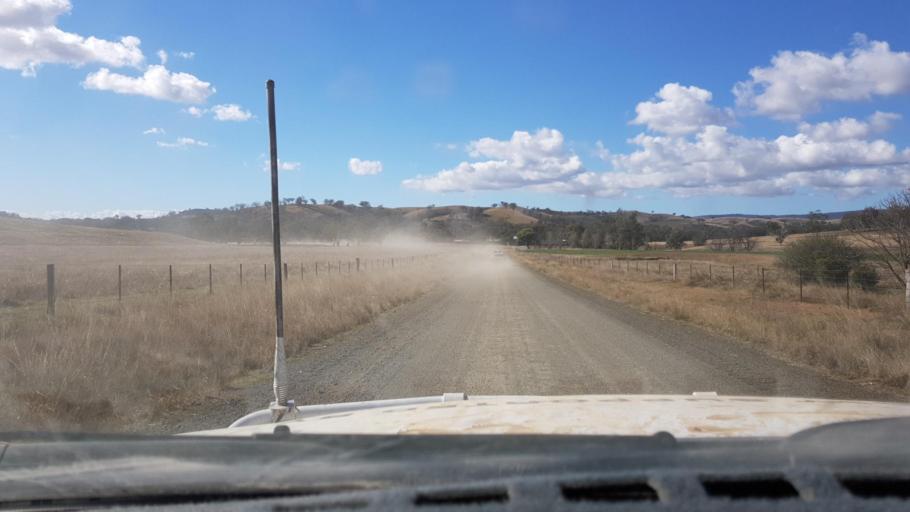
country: AU
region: New South Wales
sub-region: Narrabri
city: Blair Athol
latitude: -30.4757
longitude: 150.4395
